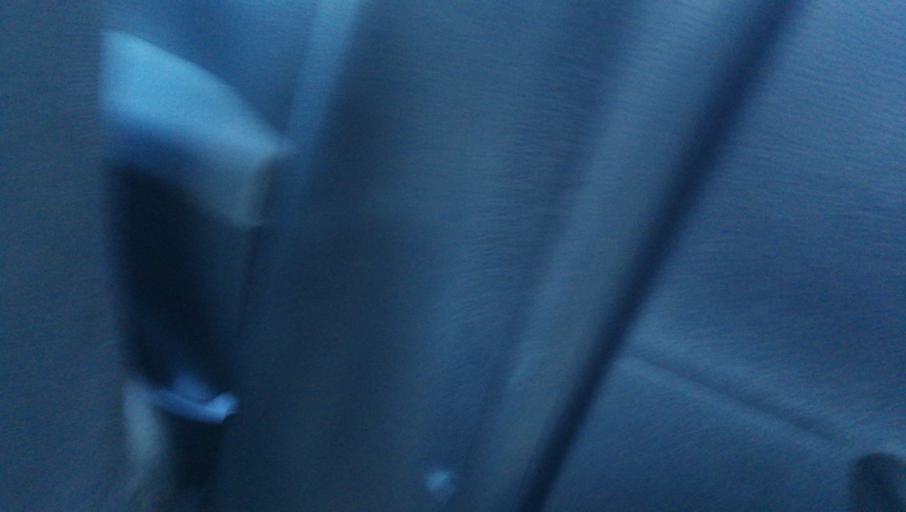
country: ET
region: Amhara
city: Were Ilu
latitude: 10.4841
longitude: 39.3017
